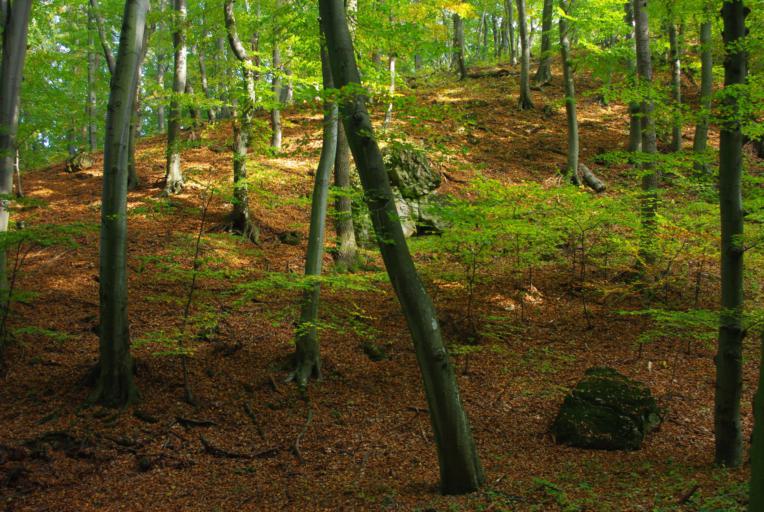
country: HU
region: Veszprem
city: Zirc
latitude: 47.3423
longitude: 17.8900
